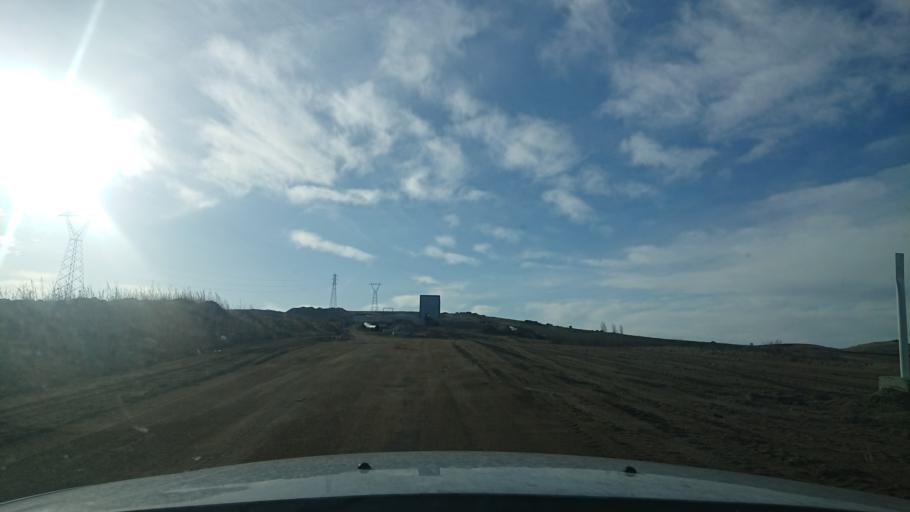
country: TR
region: Aksaray
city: Agacoren
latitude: 38.8492
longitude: 33.9432
